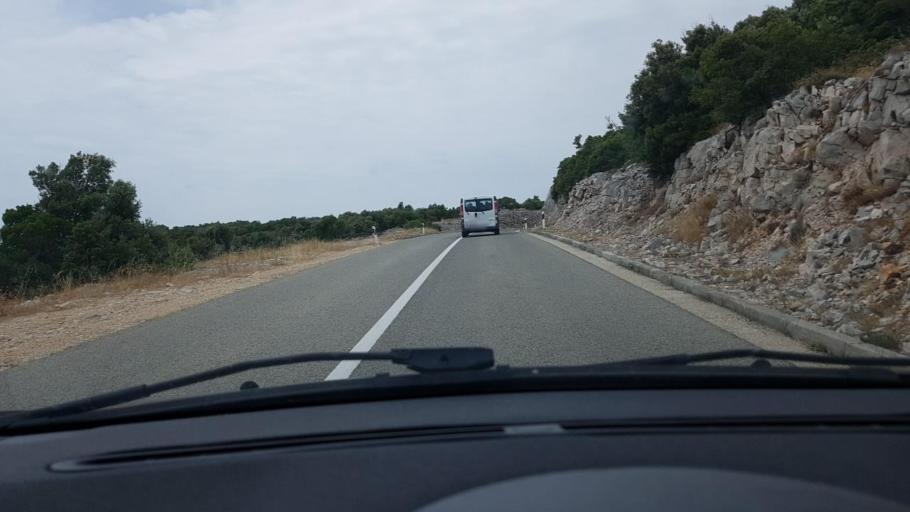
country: HR
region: Dubrovacko-Neretvanska
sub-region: Grad Korcula
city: Zrnovo
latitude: 42.9391
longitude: 17.0091
